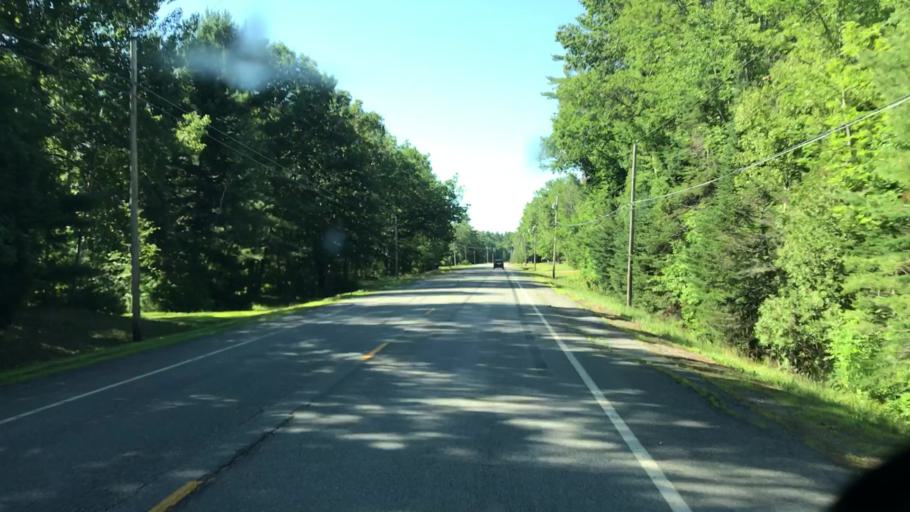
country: US
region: Maine
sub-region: Penobscot County
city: Howland
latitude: 45.2605
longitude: -68.6381
